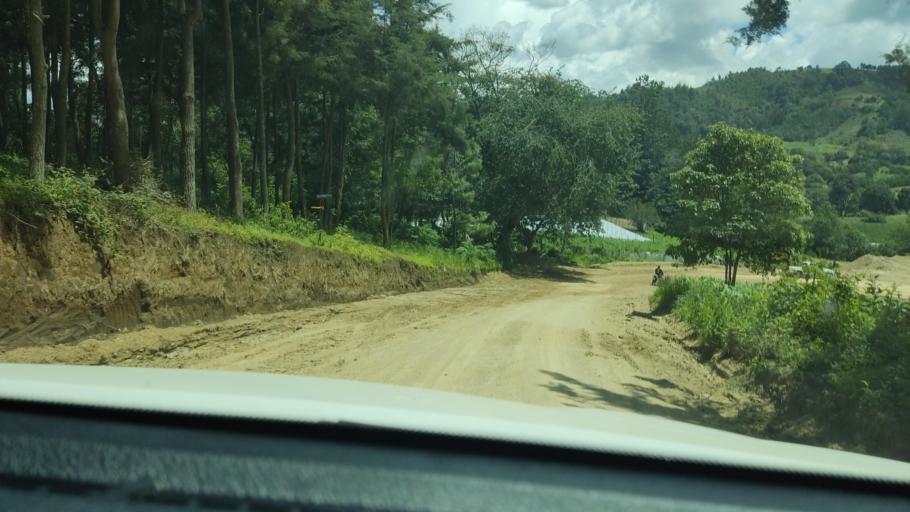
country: GT
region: Chimaltenango
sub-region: Municipio de San Juan Comalapa
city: Comalapa
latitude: 14.7648
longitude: -90.8820
